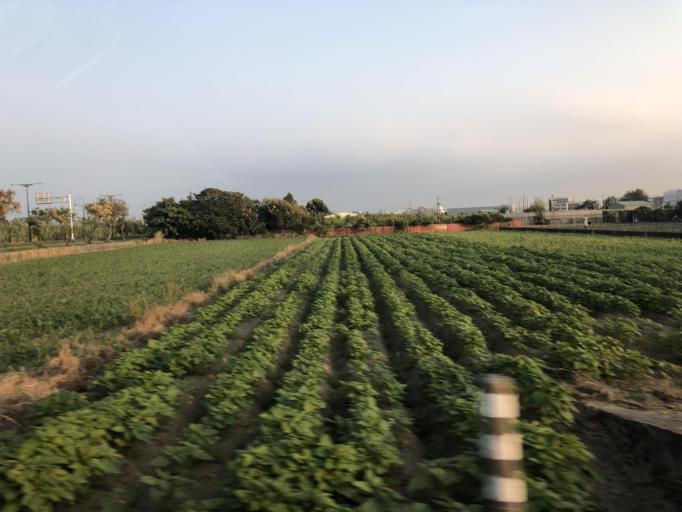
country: TW
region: Taiwan
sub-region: Tainan
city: Tainan
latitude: 23.1372
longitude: 120.2637
